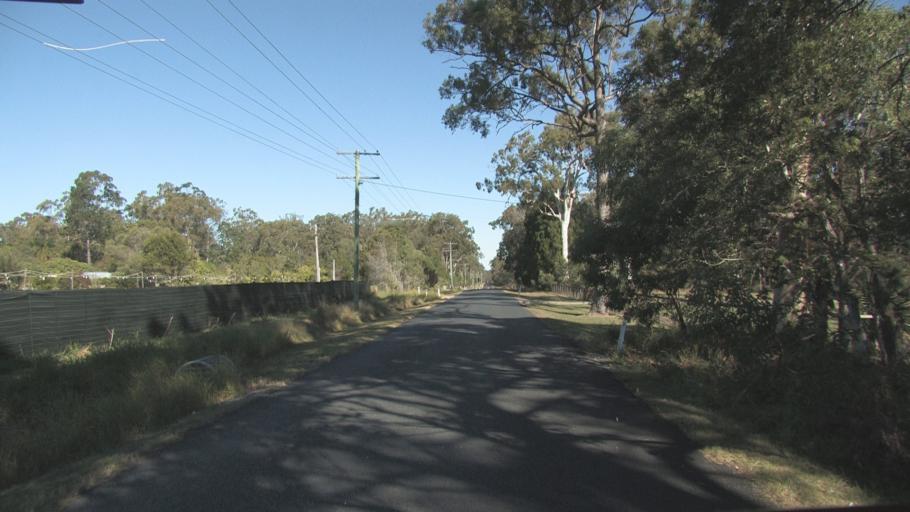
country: AU
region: Queensland
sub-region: Logan
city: Logan Reserve
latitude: -27.7256
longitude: 153.0731
